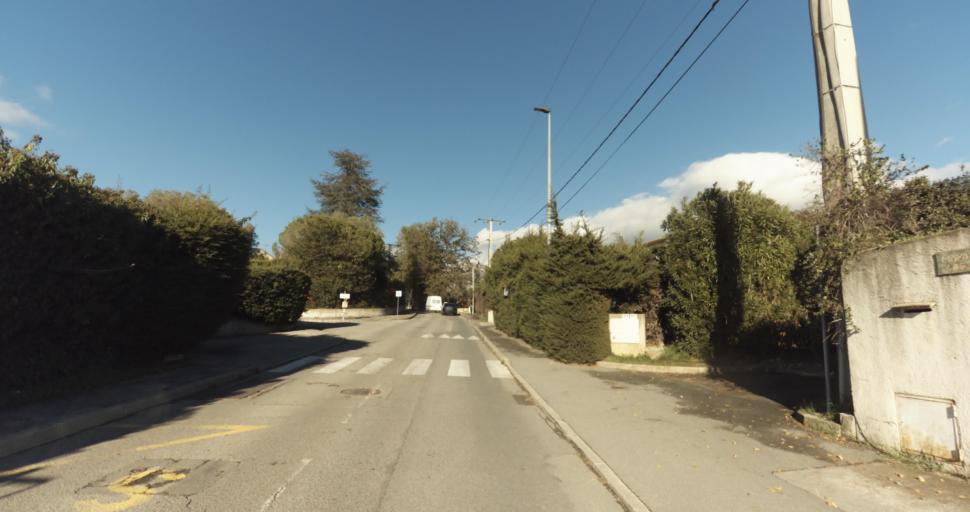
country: FR
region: Provence-Alpes-Cote d'Azur
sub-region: Departement des Alpes-Maritimes
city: Vence
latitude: 43.7149
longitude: 7.1298
